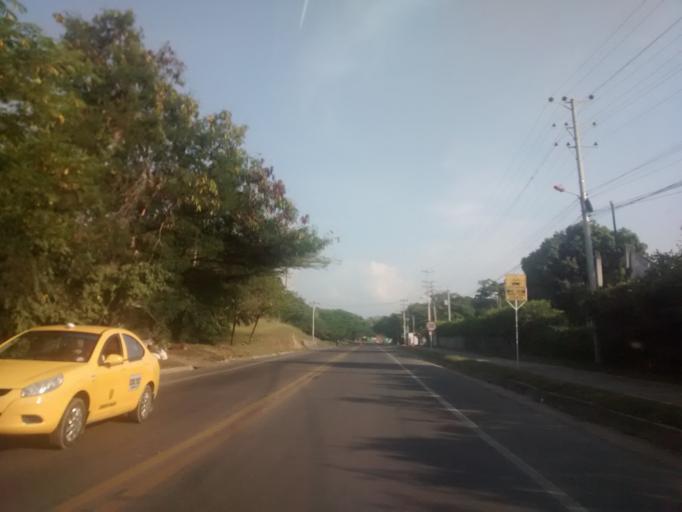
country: CO
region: Cundinamarca
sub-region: Girardot
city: Girardot City
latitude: 4.3001
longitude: -74.7925
